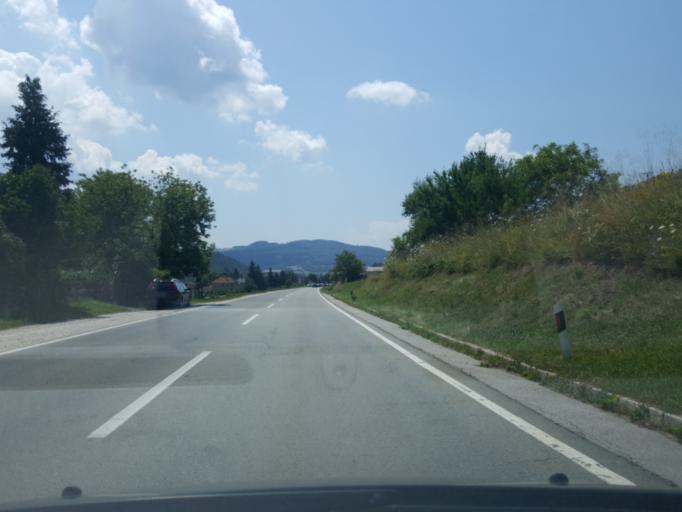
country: RS
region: Central Serbia
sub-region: Moravicki Okrug
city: Gornji Milanovac
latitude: 44.0664
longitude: 20.4912
